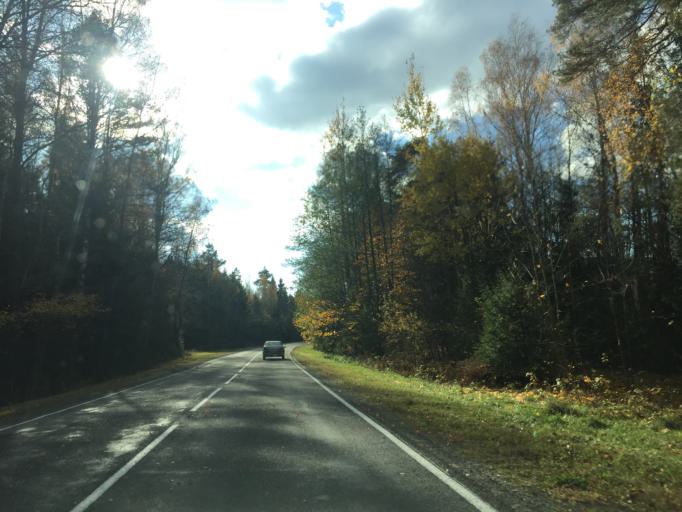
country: BY
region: Minsk
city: Narach
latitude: 54.9358
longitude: 26.5639
